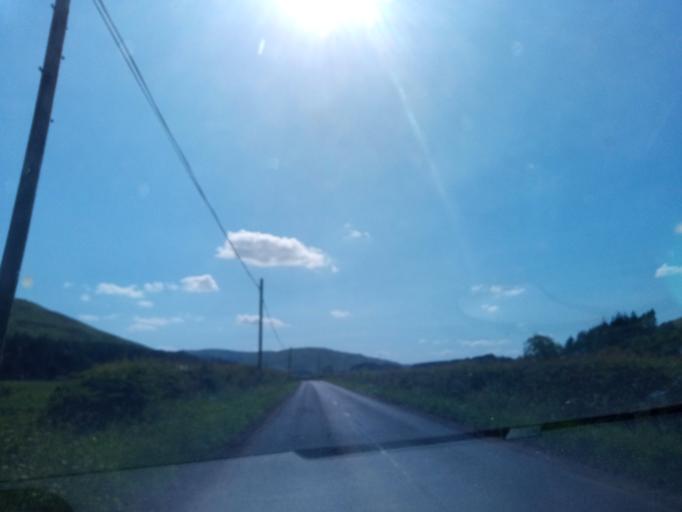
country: GB
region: Scotland
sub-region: The Scottish Borders
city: Innerleithen
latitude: 55.5164
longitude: -3.0858
